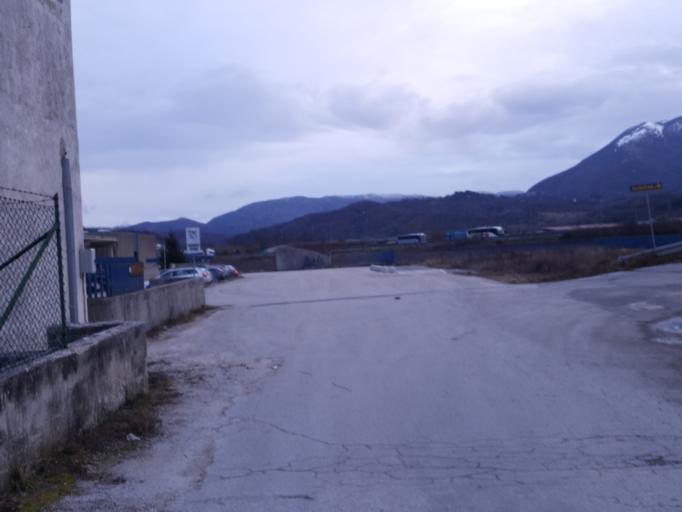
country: IT
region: Abruzzo
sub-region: Provincia dell' Aquila
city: Oricola
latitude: 42.0848
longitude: 13.0529
